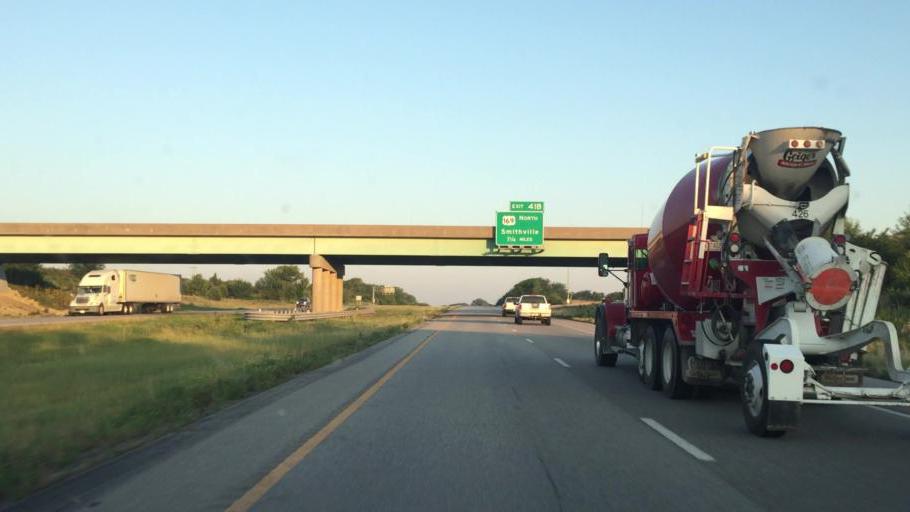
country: US
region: Missouri
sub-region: Clay County
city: Smithville
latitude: 39.3114
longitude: -94.5558
